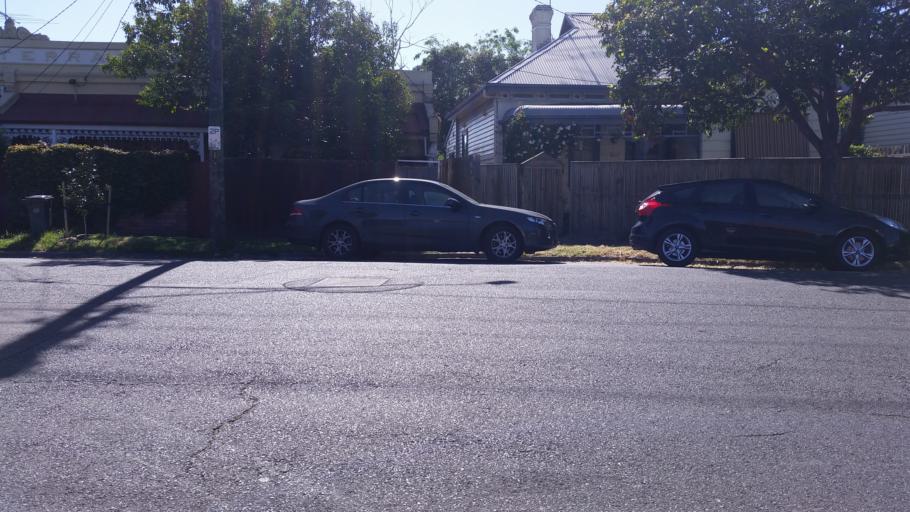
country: AU
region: Victoria
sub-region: Yarra
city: Richmond
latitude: -37.8139
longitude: 145.0079
